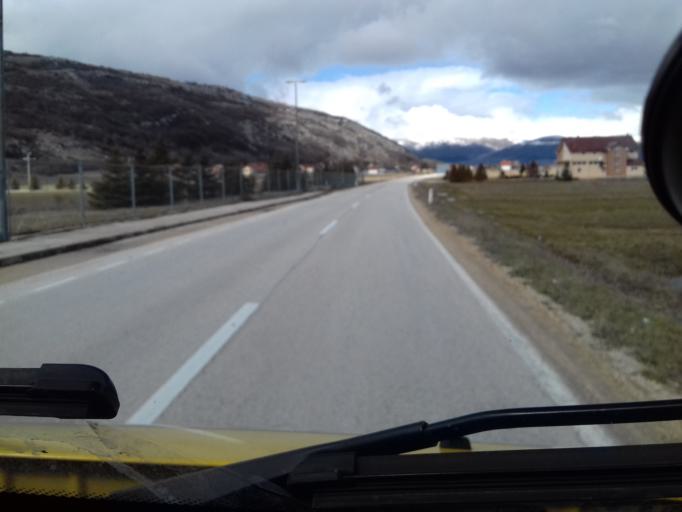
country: BA
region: Federation of Bosnia and Herzegovina
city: Tomislavgrad
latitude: 43.6530
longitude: 17.2194
